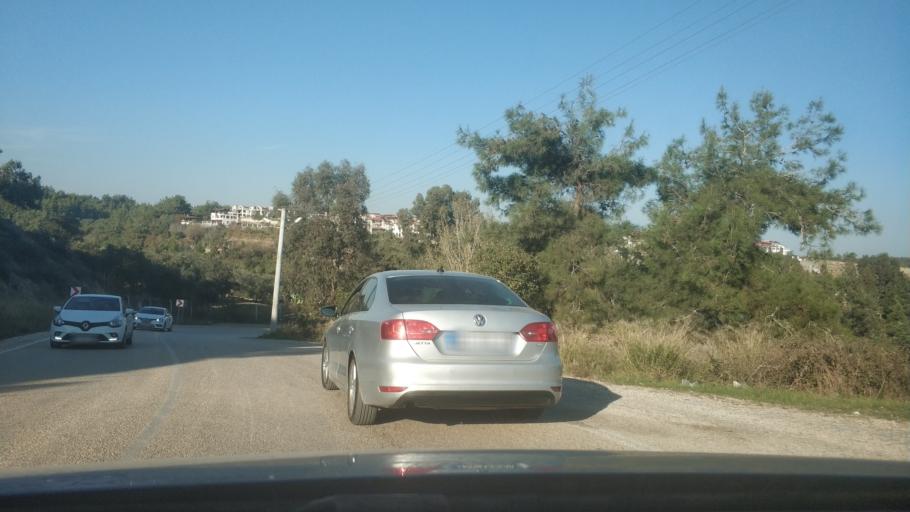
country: TR
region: Adana
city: Adana
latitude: 37.1036
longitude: 35.2946
